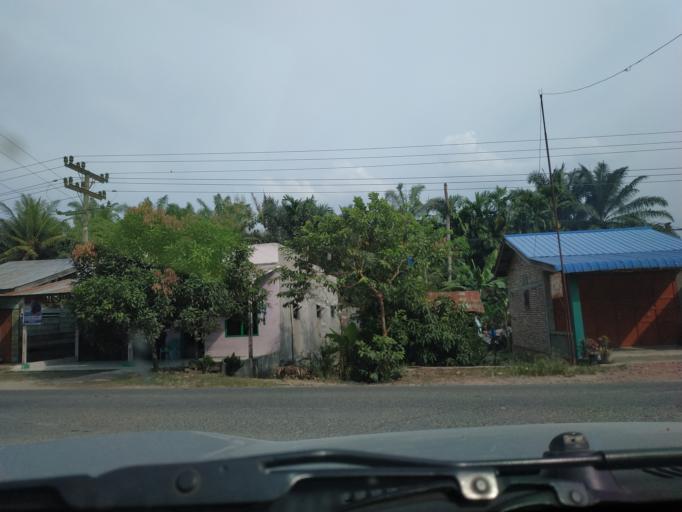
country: ID
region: North Sumatra
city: Rantauprapat
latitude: 2.1865
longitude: 100.0319
